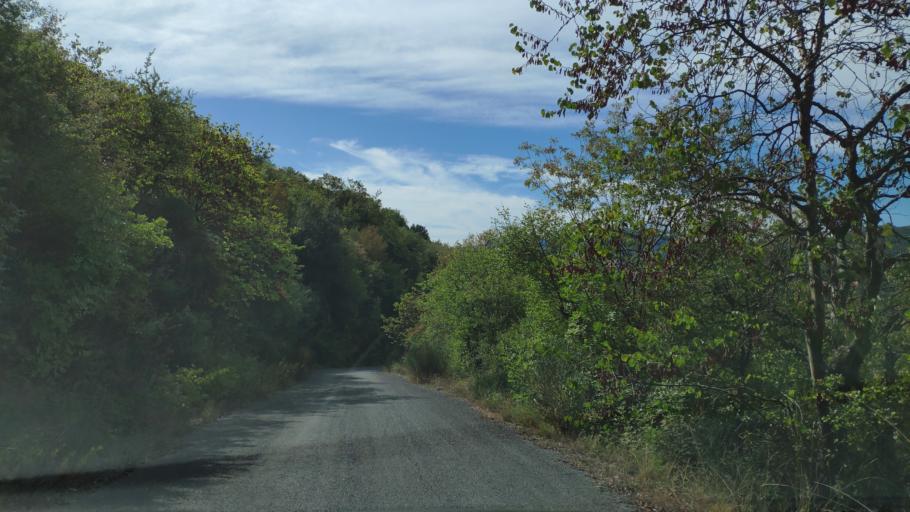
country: GR
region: Peloponnese
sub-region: Nomos Arkadias
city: Dimitsana
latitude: 37.5417
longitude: 22.0516
